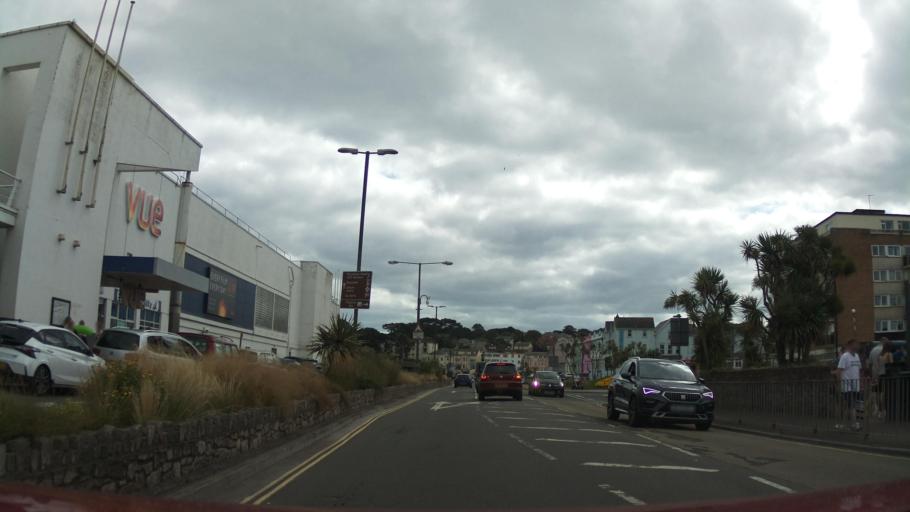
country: GB
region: England
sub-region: Borough of Torbay
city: Paignton
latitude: 50.4357
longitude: -3.5603
